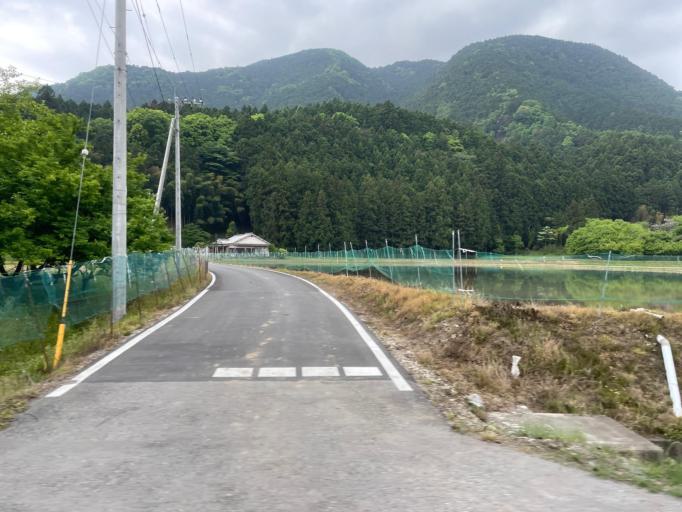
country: JP
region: Tochigi
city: Tanuma
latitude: 36.4647
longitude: 139.6354
